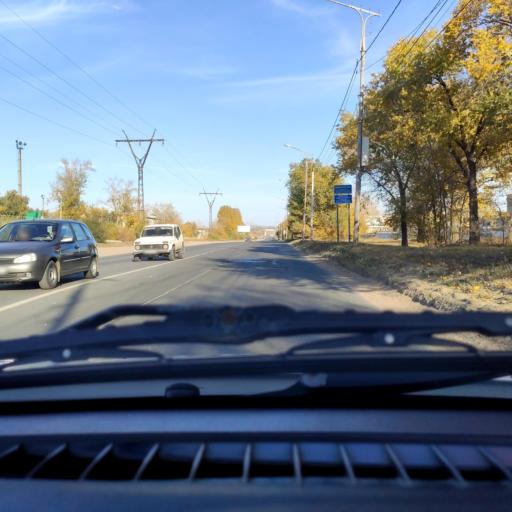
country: RU
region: Samara
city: Zhigulevsk
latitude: 53.4765
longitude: 49.4887
